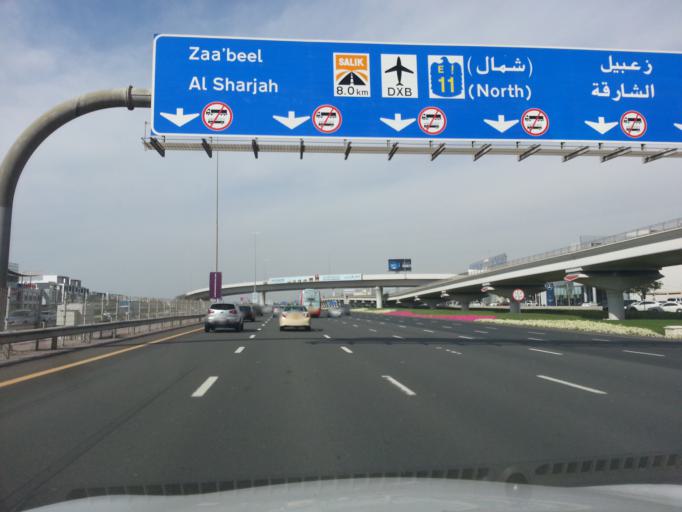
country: AE
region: Dubai
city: Dubai
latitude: 25.1378
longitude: 55.2168
